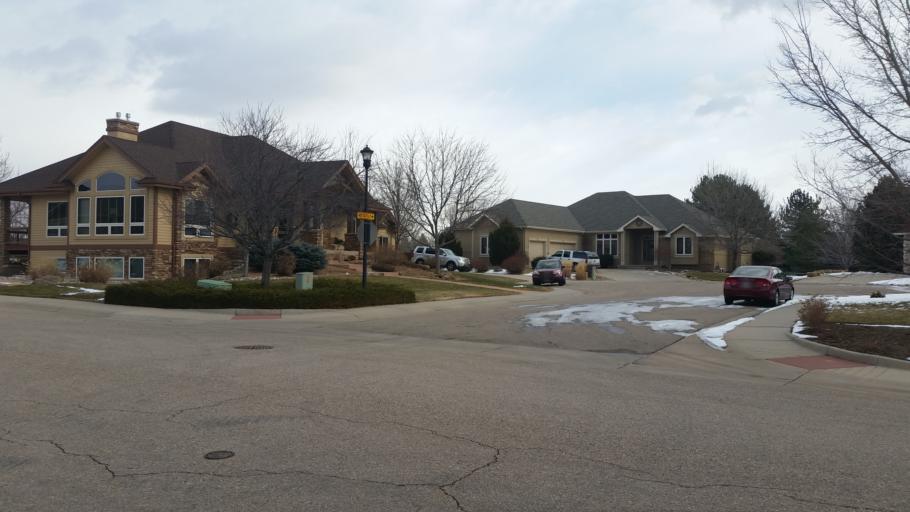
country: US
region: Colorado
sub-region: Larimer County
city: Fort Collins
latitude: 40.5217
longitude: -105.1067
